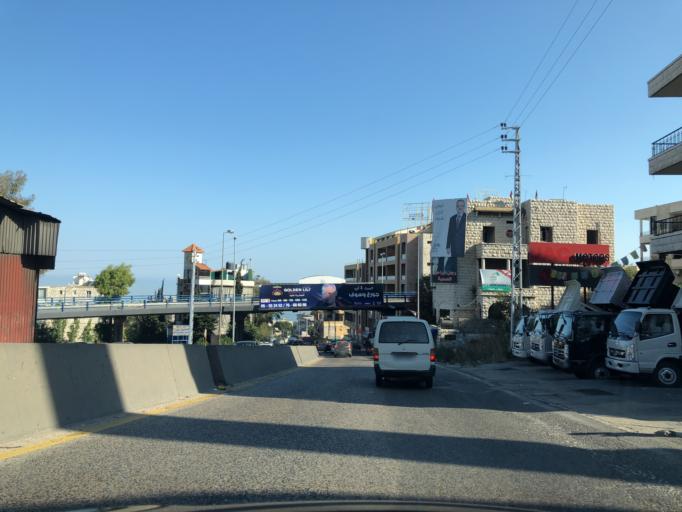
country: LB
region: Mont-Liban
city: Aaley
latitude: 33.8154
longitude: 35.6084
